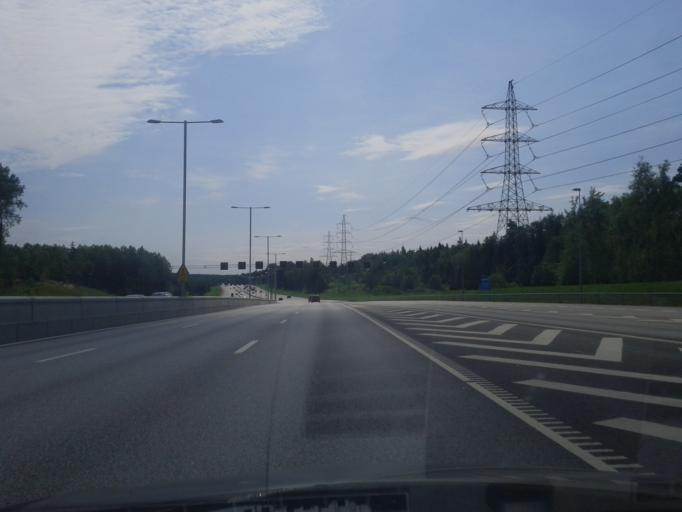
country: SE
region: Stockholm
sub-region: Stockholms Kommun
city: Kista
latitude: 59.3998
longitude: 17.9760
